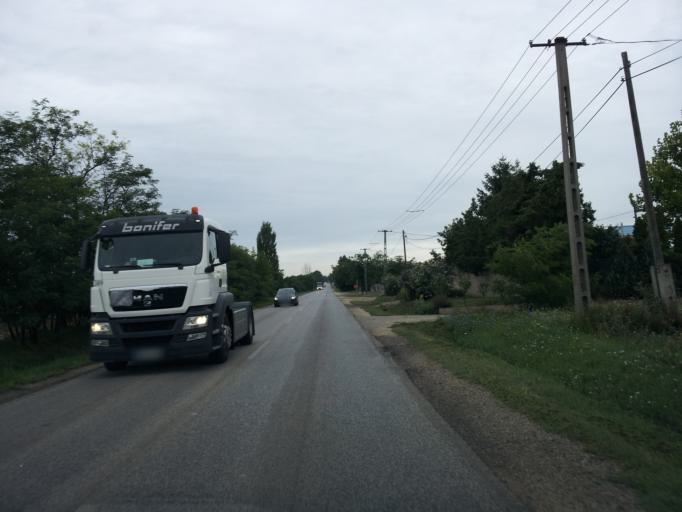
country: HU
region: Pest
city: Tarnok
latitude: 47.3840
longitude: 18.8625
